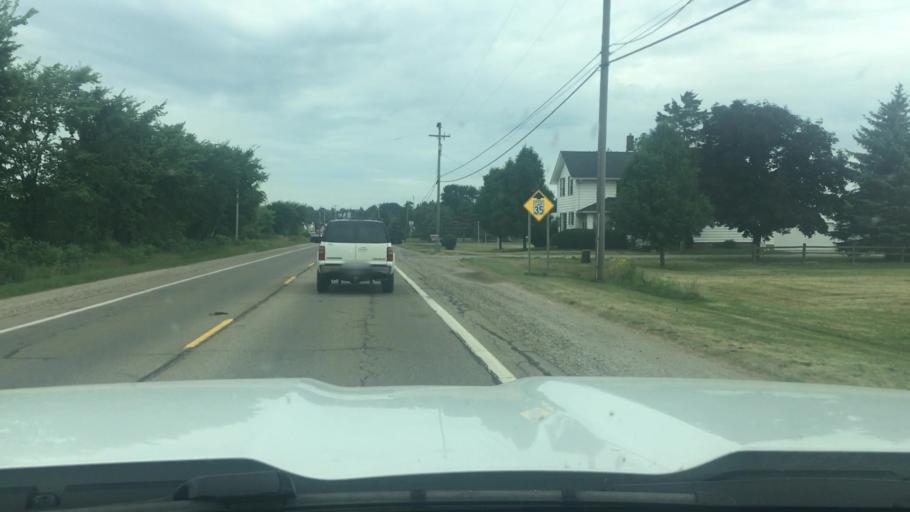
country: US
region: Michigan
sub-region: Clinton County
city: Saint Johns
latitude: 43.0014
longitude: -84.5379
